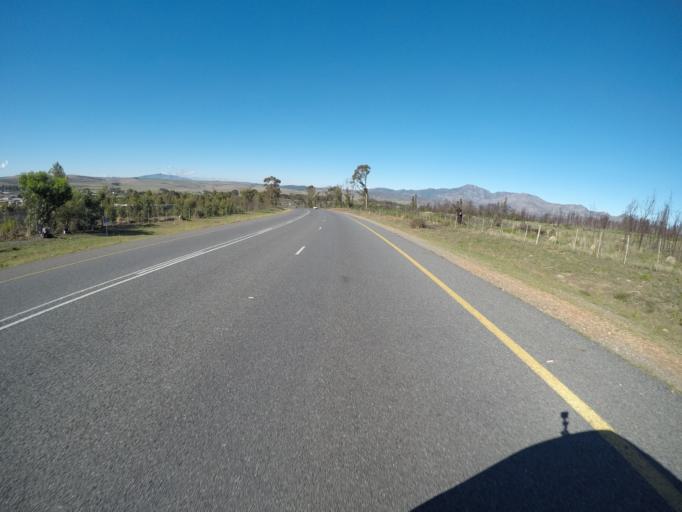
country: ZA
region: Western Cape
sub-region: Overberg District Municipality
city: Hermanus
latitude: -34.2344
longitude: 19.1913
